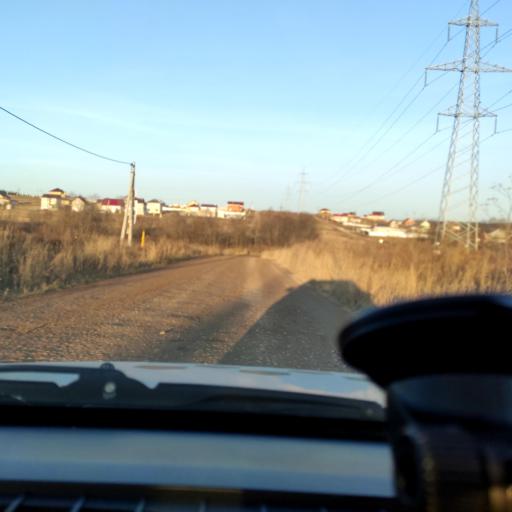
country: RU
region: Perm
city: Ferma
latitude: 57.9460
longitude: 56.3522
